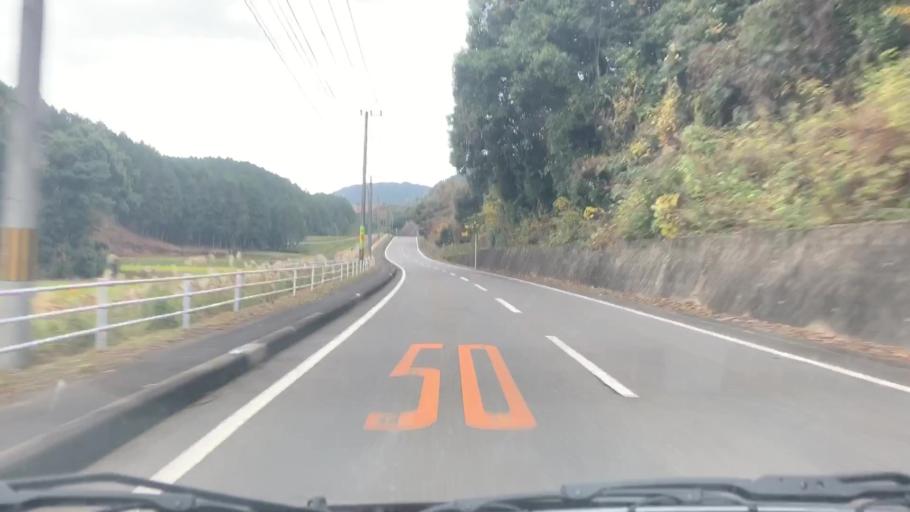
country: JP
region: Saga Prefecture
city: Ureshinomachi-shimojuku
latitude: 33.1176
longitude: 129.9774
